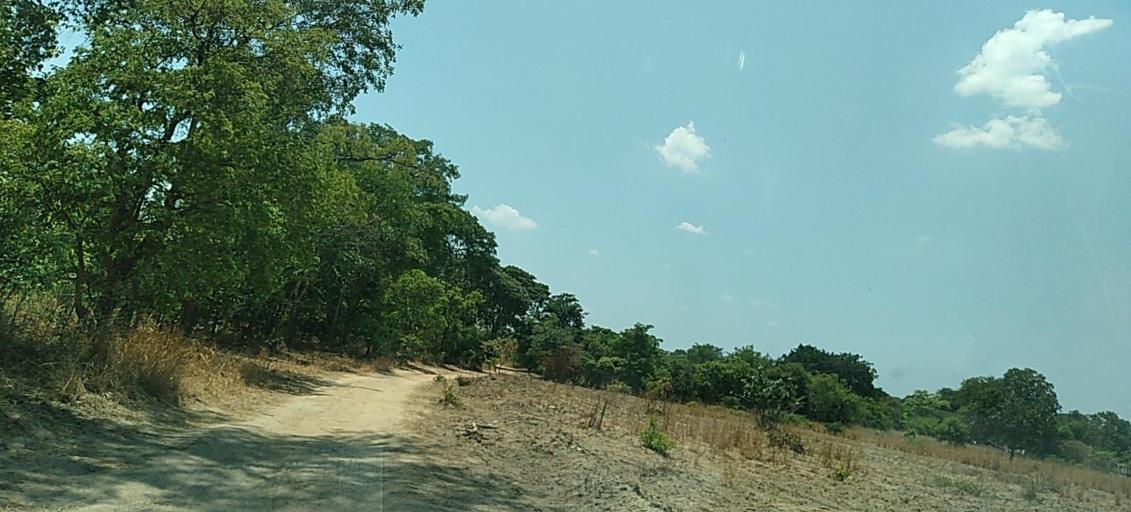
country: ZM
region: Central
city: Kapiri Mposhi
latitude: -13.6699
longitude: 28.4974
